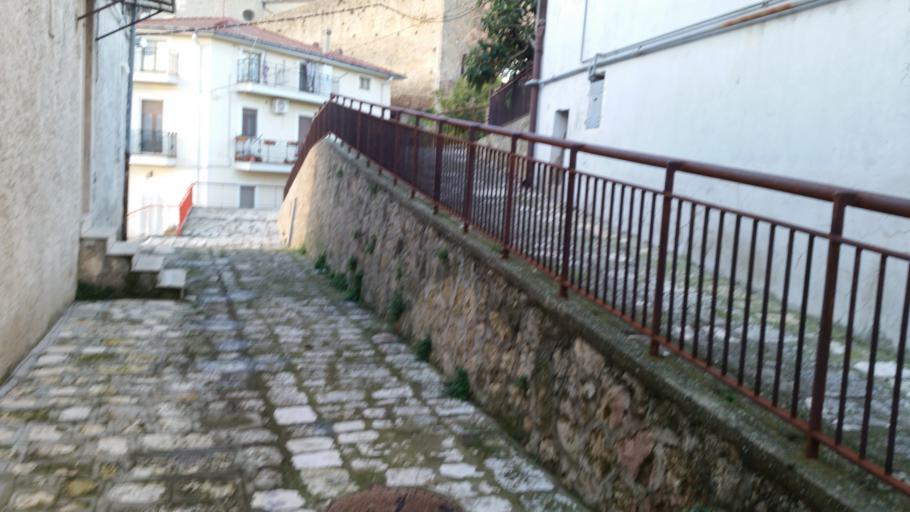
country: IT
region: Basilicate
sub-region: Provincia di Matera
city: Tricarico
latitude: 40.6200
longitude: 16.1474
